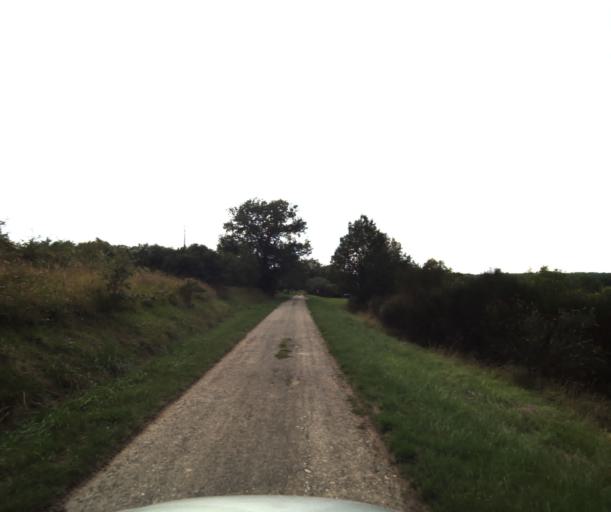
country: FR
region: Midi-Pyrenees
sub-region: Departement de la Haute-Garonne
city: Eaunes
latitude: 43.4396
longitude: 1.3624
